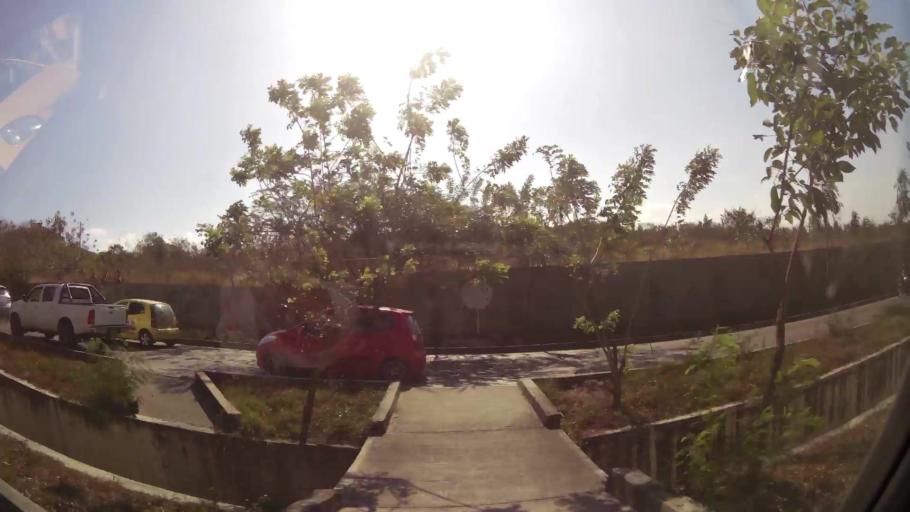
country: CO
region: Atlantico
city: Barranquilla
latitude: 10.9898
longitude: -74.8282
